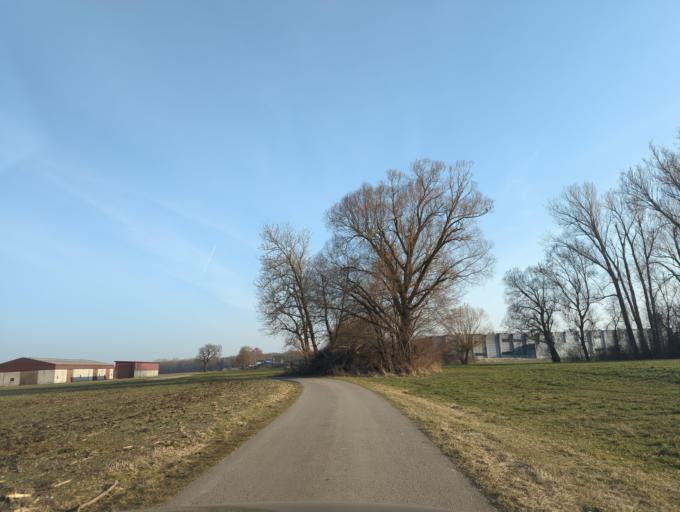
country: DE
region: Bavaria
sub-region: Swabia
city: Leipheim
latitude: 48.4645
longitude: 10.2112
